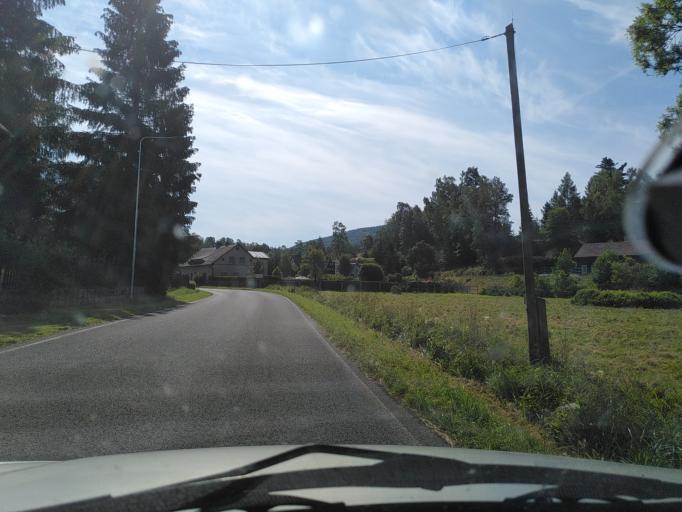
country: CZ
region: Ustecky
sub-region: Okres Decin
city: Chribska
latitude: 50.8159
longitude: 14.5267
